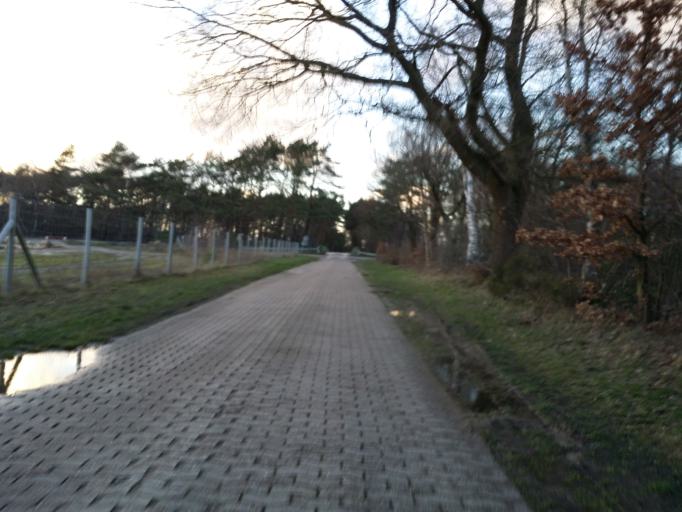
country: DE
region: Lower Saxony
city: Gross Ippener
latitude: 52.9647
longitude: 8.6004
